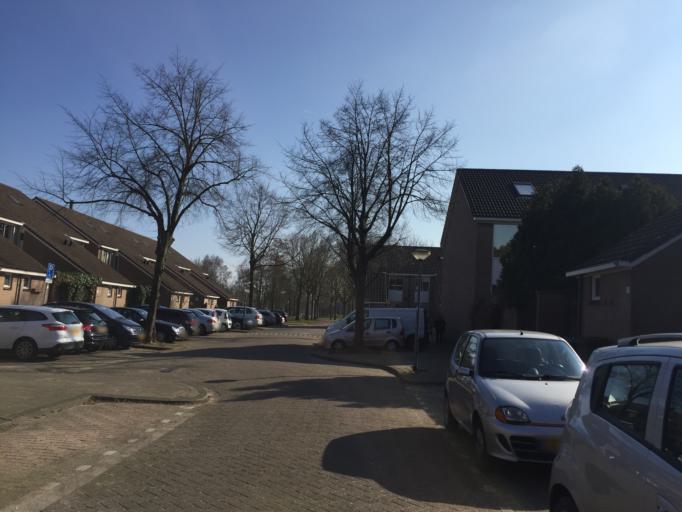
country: NL
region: South Holland
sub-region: Gemeente Capelle aan den IJssel
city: Capelle aan den IJssel
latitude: 51.9442
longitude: 4.5693
